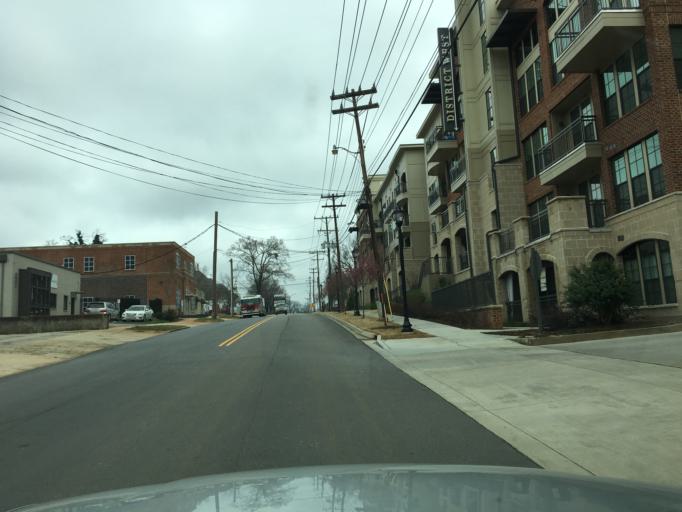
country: US
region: South Carolina
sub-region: Greenville County
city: Greenville
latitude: 34.8493
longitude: -82.4064
